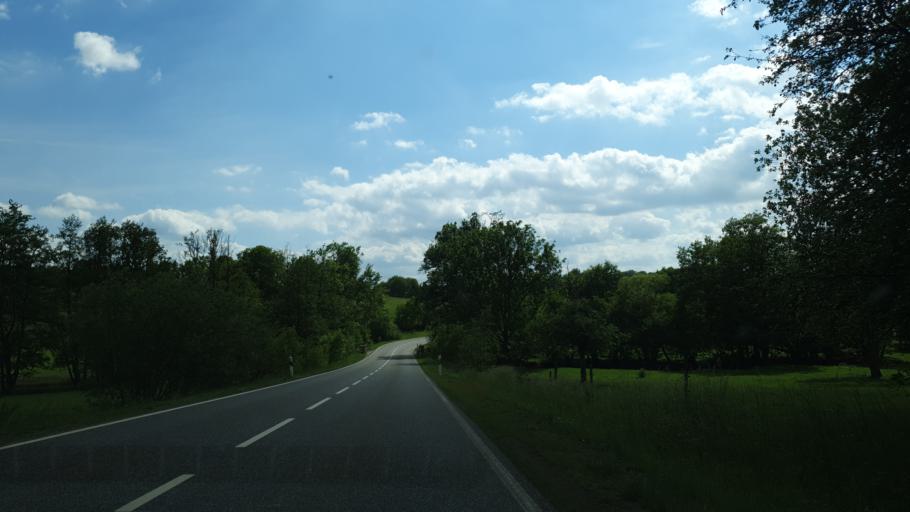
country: DE
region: Rheinland-Pfalz
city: Helferskirchen
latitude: 50.5192
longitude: 7.8171
